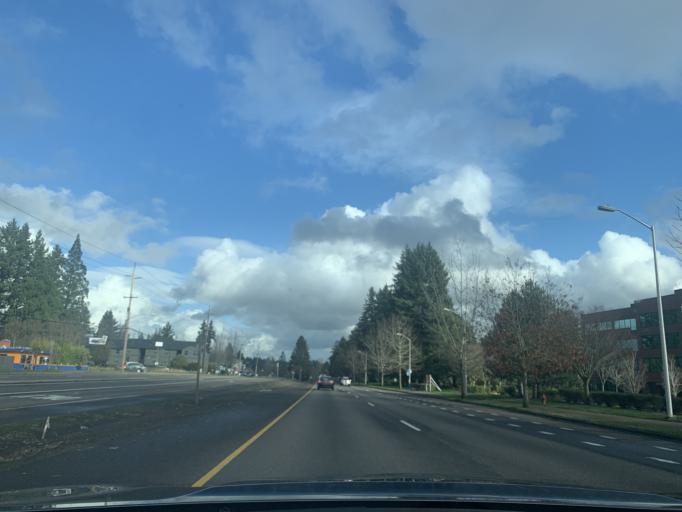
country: US
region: Oregon
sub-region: Washington County
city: King City
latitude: 45.3894
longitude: -122.8050
